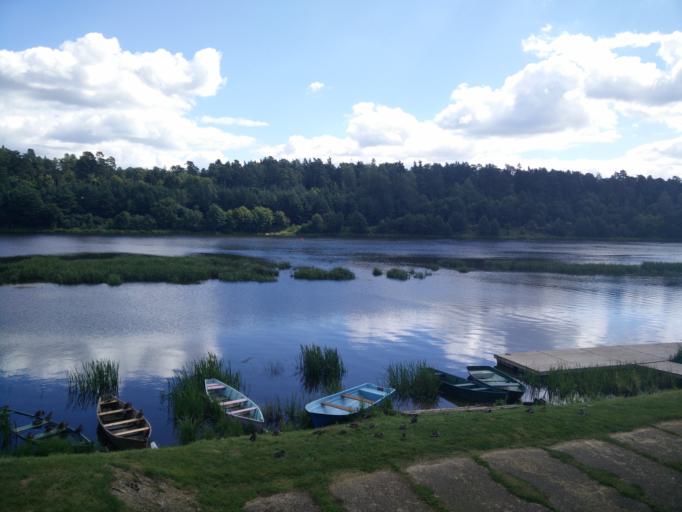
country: LT
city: Birstonas
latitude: 54.6030
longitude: 24.0365
